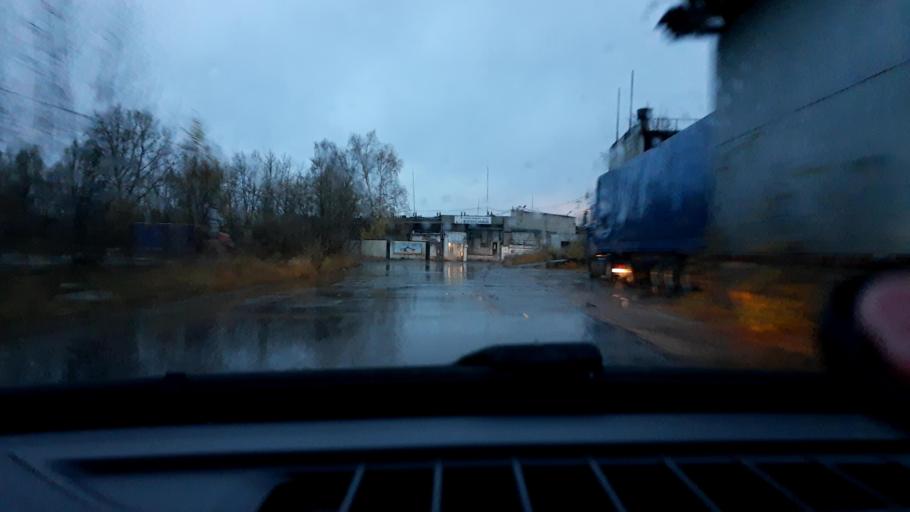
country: RU
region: Nizjnij Novgorod
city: Gorbatovka
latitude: 56.3395
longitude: 43.8192
